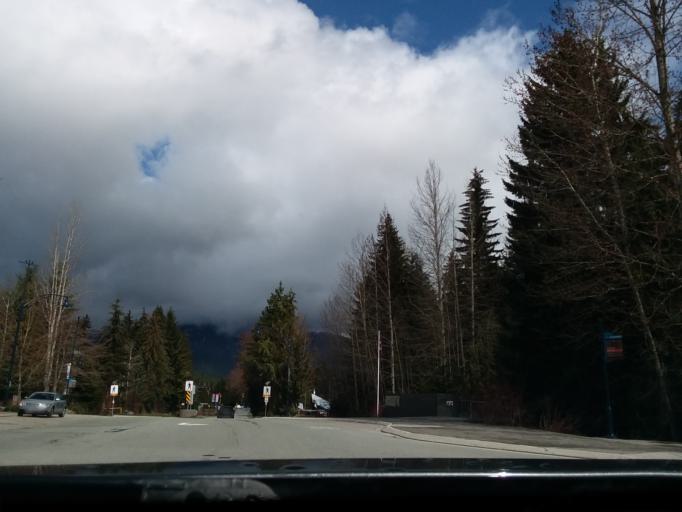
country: CA
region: British Columbia
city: Whistler
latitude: 50.1176
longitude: -122.9537
